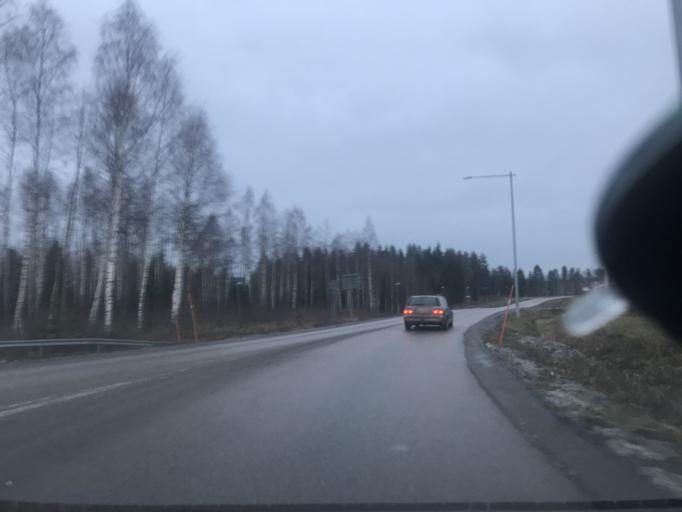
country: SE
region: Norrbotten
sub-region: Lulea Kommun
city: Bergnaset
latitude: 65.6127
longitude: 22.1180
